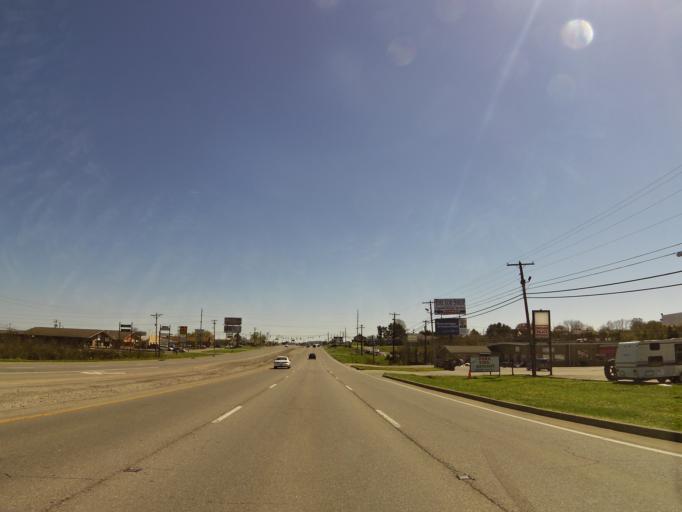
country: US
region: Kentucky
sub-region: Pulaski County
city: Somerset
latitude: 37.0455
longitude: -84.6261
